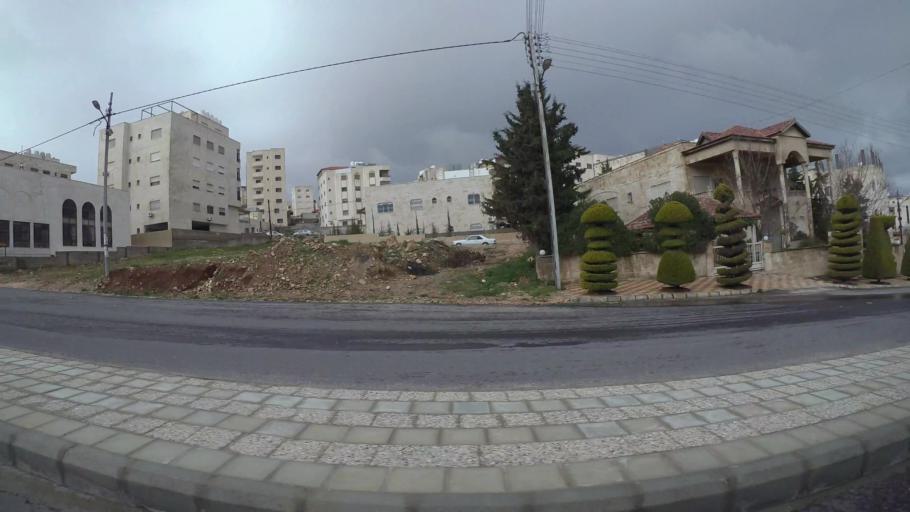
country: JO
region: Amman
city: Al Jubayhah
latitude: 32.0607
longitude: 35.8914
